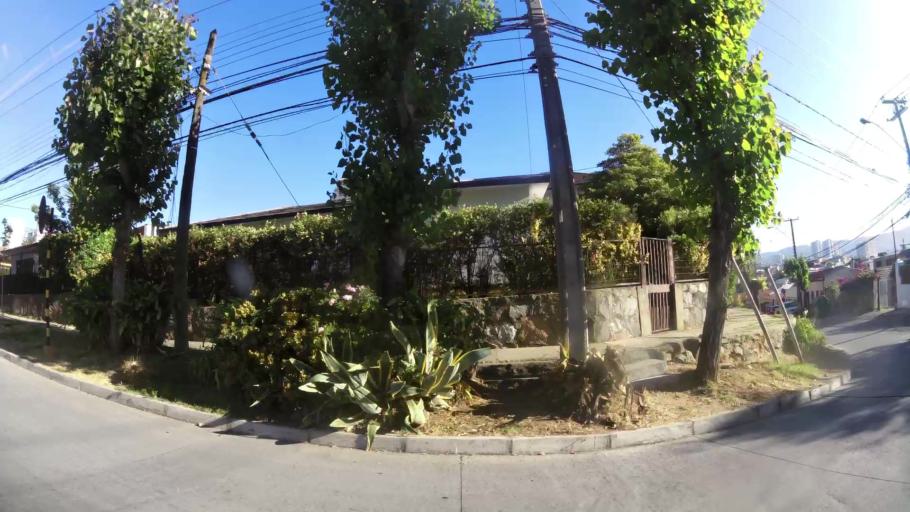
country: CL
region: Valparaiso
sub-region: Provincia de Valparaiso
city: Vina del Mar
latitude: -33.0283
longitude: -71.5841
